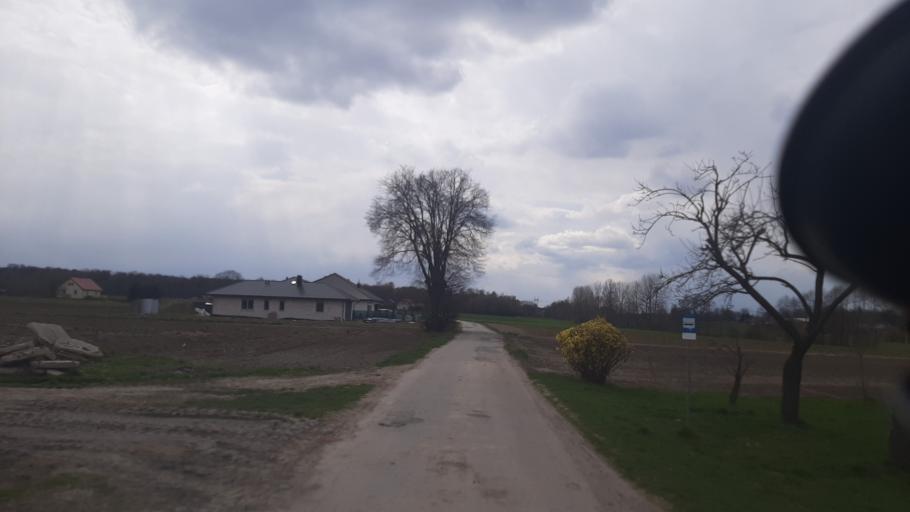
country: PL
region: Lublin Voivodeship
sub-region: Powiat lubelski
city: Jastkow
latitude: 51.3580
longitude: 22.4419
